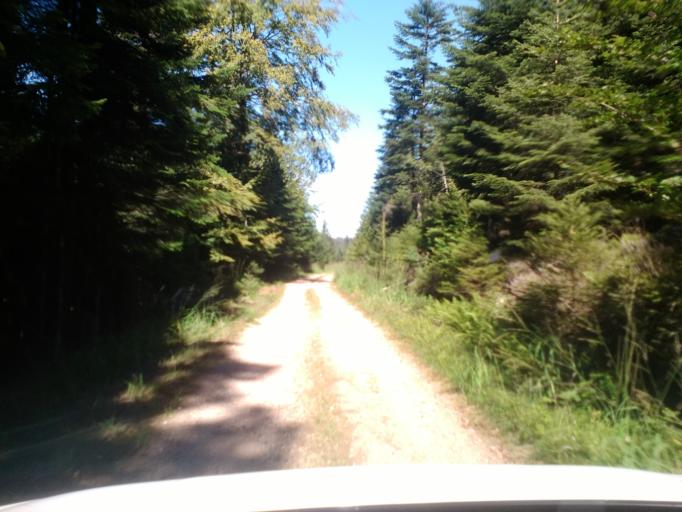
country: FR
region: Lorraine
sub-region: Departement des Vosges
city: Senones
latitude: 48.4265
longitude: 6.9900
